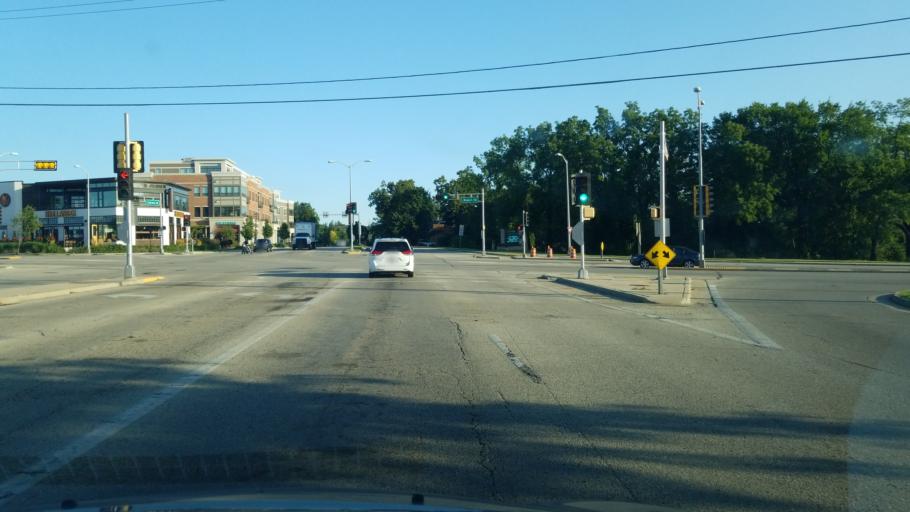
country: US
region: Wisconsin
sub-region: Ozaukee County
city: Mequon
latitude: 43.2211
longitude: -87.9823
